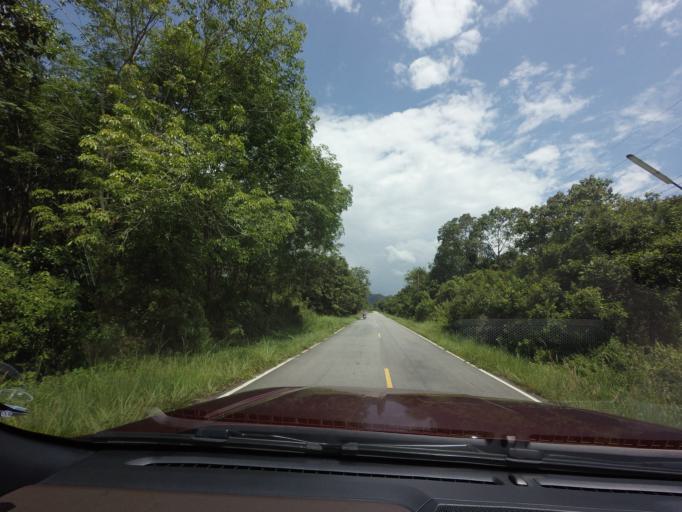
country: TH
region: Narathiwat
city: Chanae
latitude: 6.0844
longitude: 101.6904
